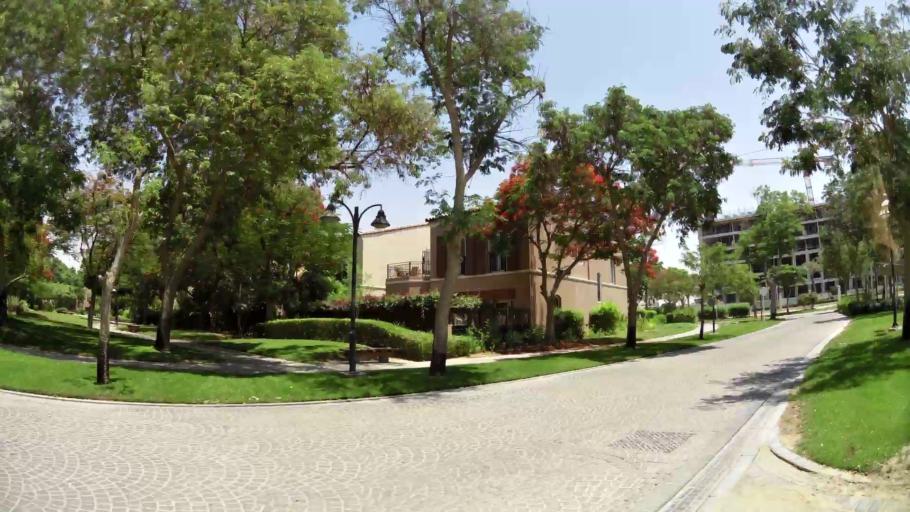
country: AE
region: Dubai
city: Dubai
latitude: 25.0030
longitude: 55.1565
